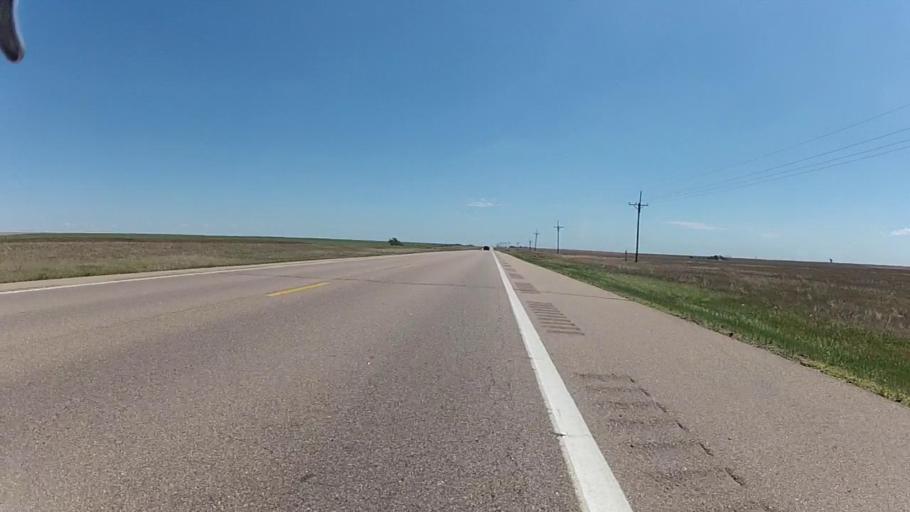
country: US
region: Kansas
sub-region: Ford County
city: Dodge City
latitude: 37.6983
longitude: -100.1551
